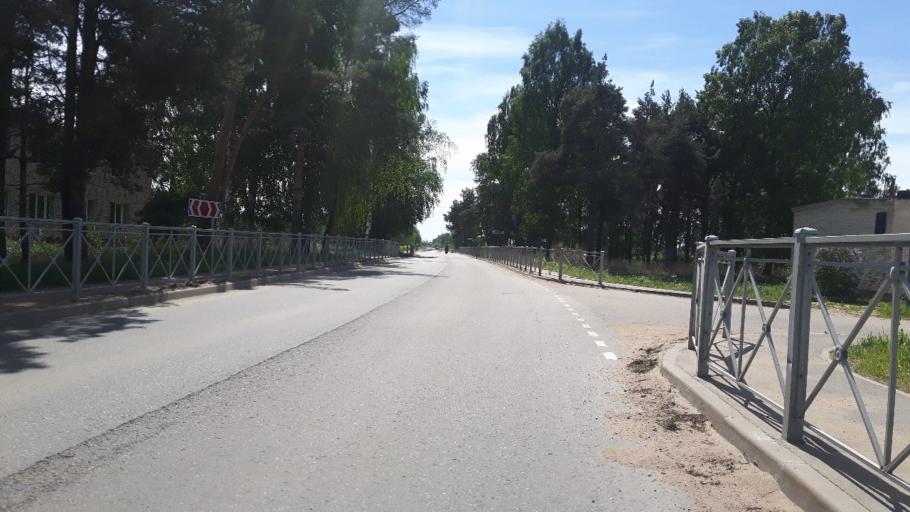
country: RU
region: Leningrad
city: Ust'-Luga
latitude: 59.5788
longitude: 28.1767
